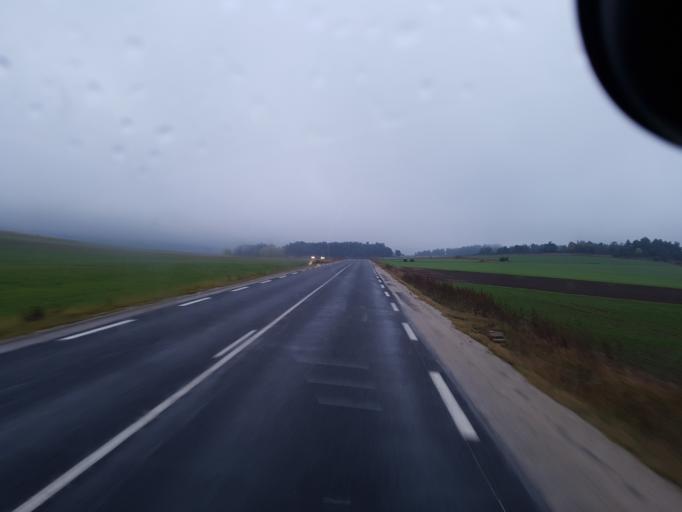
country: FR
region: Languedoc-Roussillon
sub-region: Departement de la Lozere
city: Langogne
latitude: 44.8337
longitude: 3.8620
